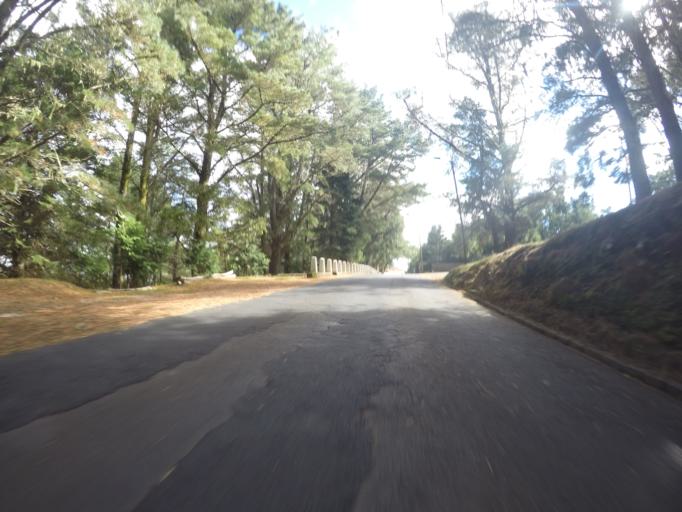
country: PT
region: Madeira
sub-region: Funchal
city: Nossa Senhora do Monte
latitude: 32.6961
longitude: -16.8786
